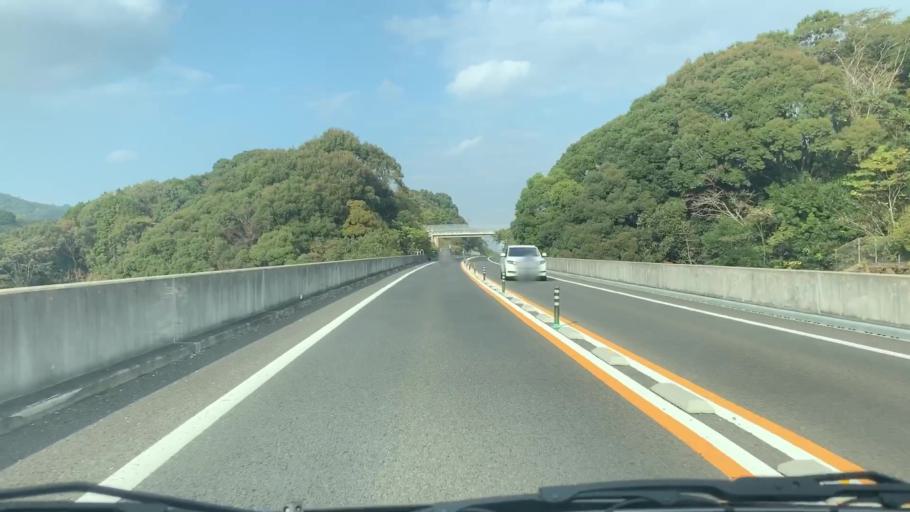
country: JP
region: Nagasaki
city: Sasebo
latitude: 33.0051
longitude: 129.7274
